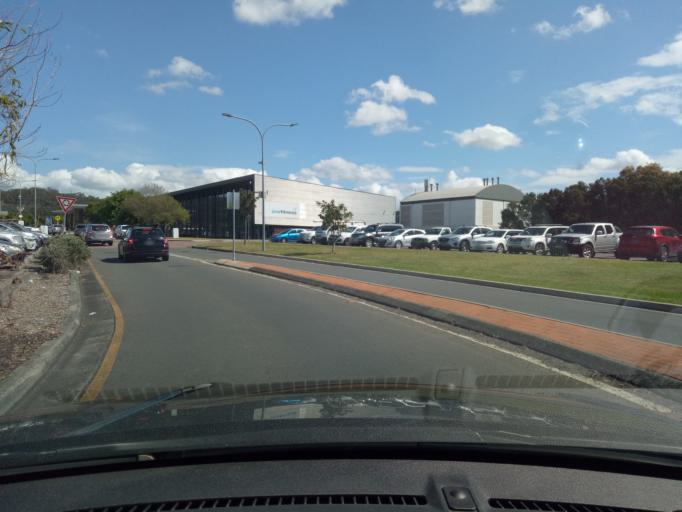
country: AU
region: New South Wales
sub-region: Wyong Shire
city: Tumbi Vmbi
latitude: -33.3631
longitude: 151.4426
